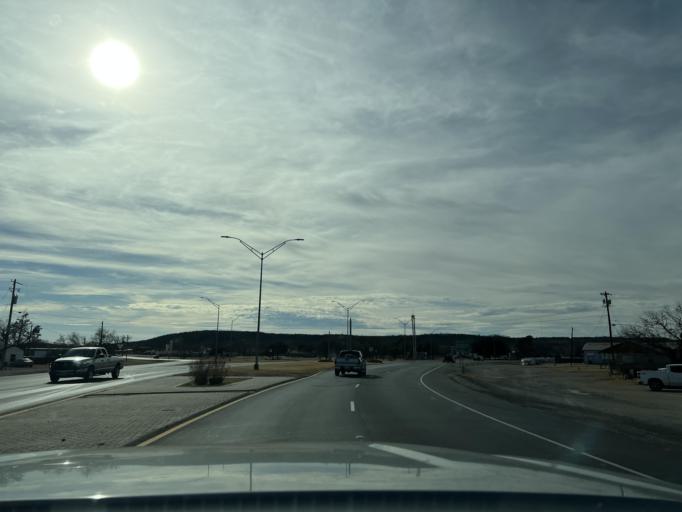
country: US
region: Texas
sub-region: Shackelford County
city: Albany
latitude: 32.7187
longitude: -99.2987
